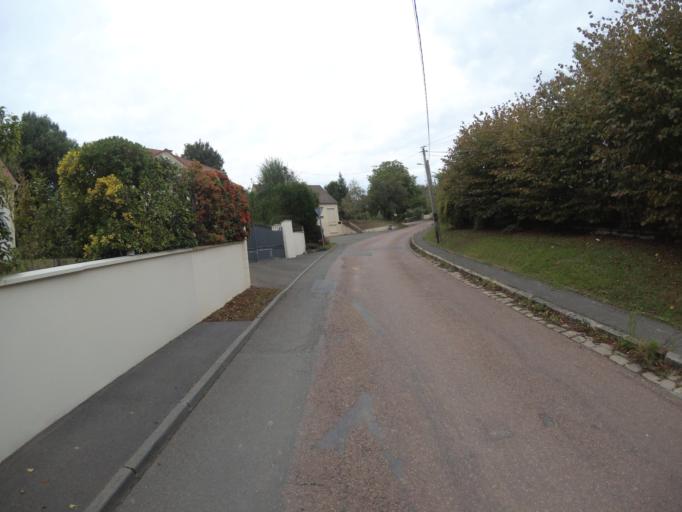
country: FR
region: Ile-de-France
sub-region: Departement de Seine-et-Marne
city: Gouvernes
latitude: 48.8611
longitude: 2.6904
